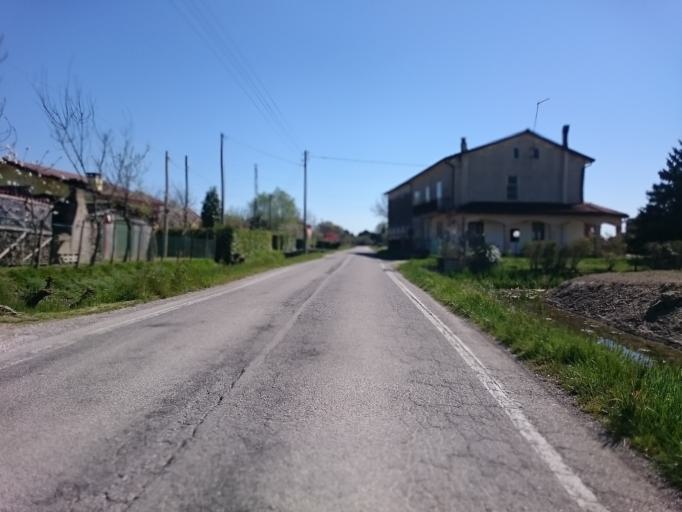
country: IT
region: Veneto
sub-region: Provincia di Padova
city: Campagnola
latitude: 45.2906
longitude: 12.0093
